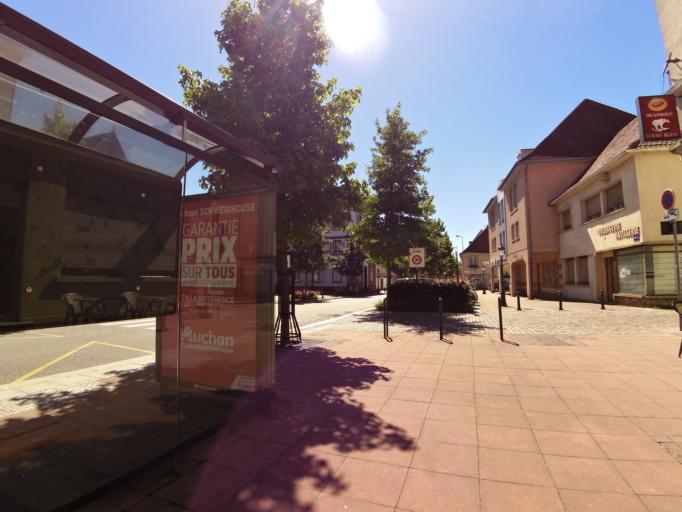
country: FR
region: Alsace
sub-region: Departement du Bas-Rhin
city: Haguenau
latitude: 48.8205
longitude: 7.7913
